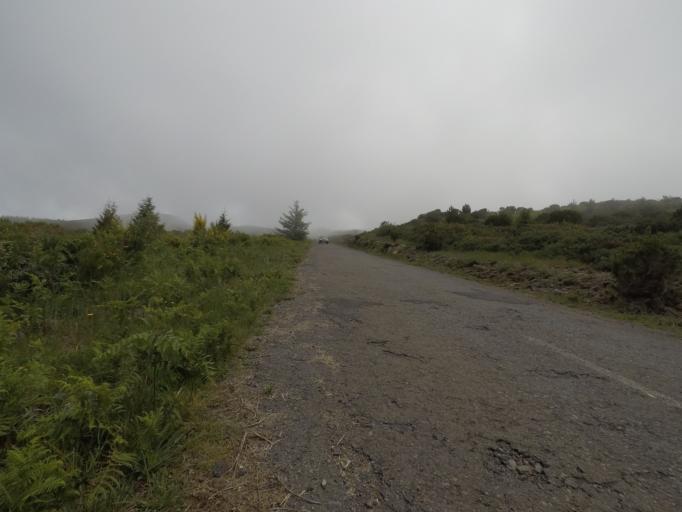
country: PT
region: Madeira
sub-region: Sao Vicente
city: Sao Vicente
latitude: 32.7654
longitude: -17.0816
